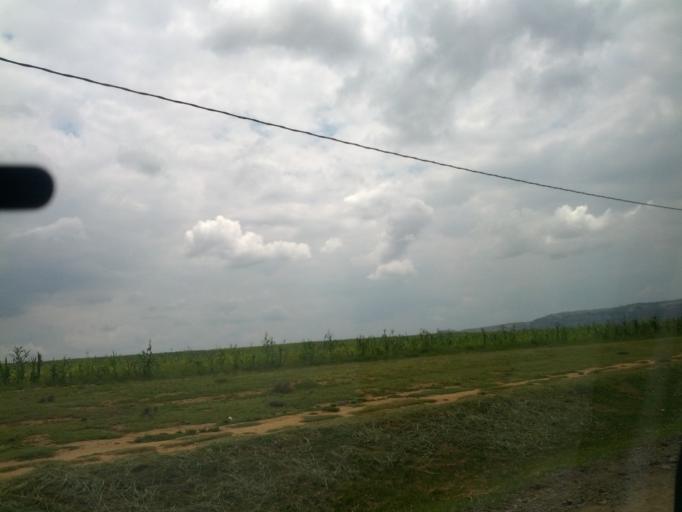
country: LS
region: Leribe
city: Leribe
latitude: -28.9329
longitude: 28.1534
